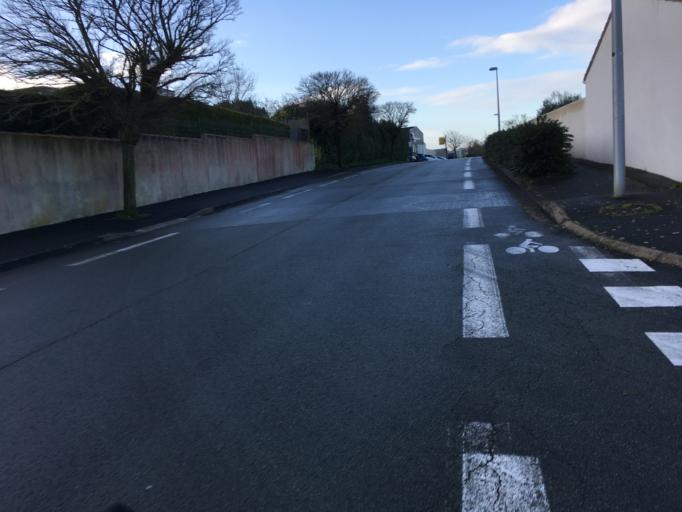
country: FR
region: Poitou-Charentes
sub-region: Departement de la Charente-Maritime
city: Nieul-sur-Mer
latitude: 46.2035
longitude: -1.1713
